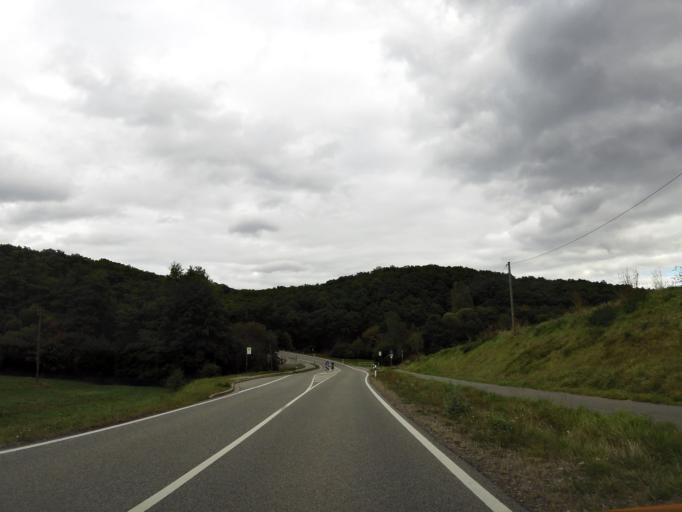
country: DE
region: Rheinland-Pfalz
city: Dannenfels
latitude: 49.6359
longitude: 7.9553
